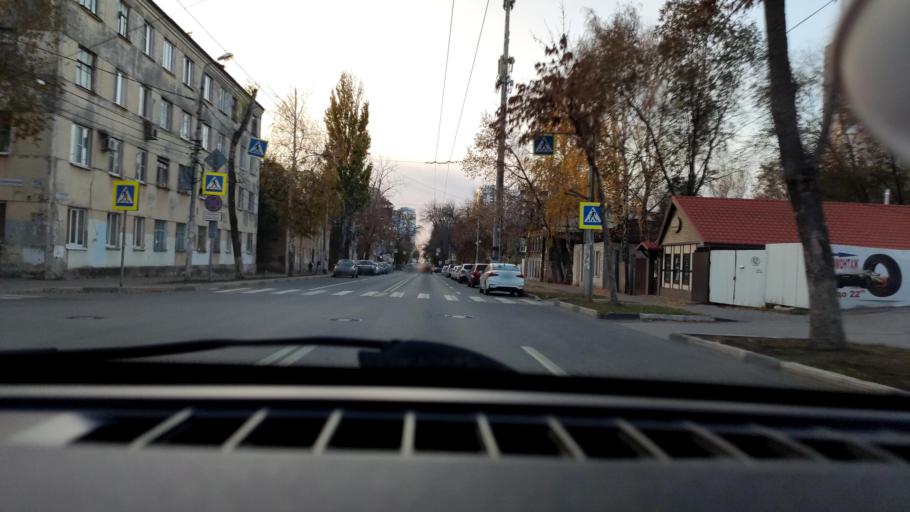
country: RU
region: Samara
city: Samara
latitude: 53.1972
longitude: 50.1164
